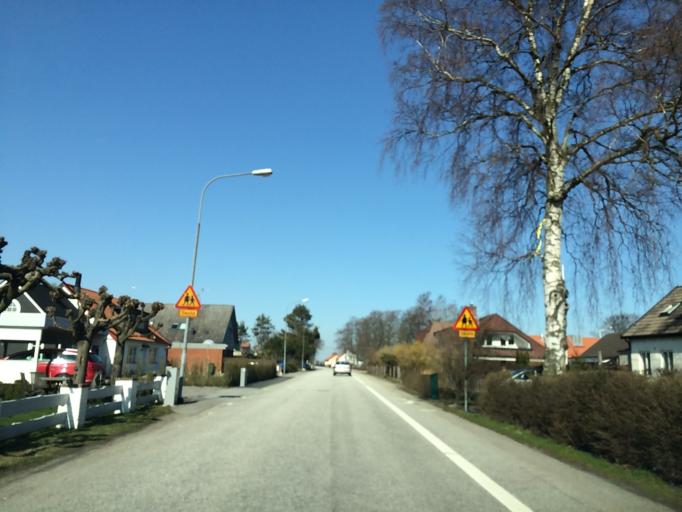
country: SE
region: Skane
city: Bjarred
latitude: 55.7365
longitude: 13.0316
